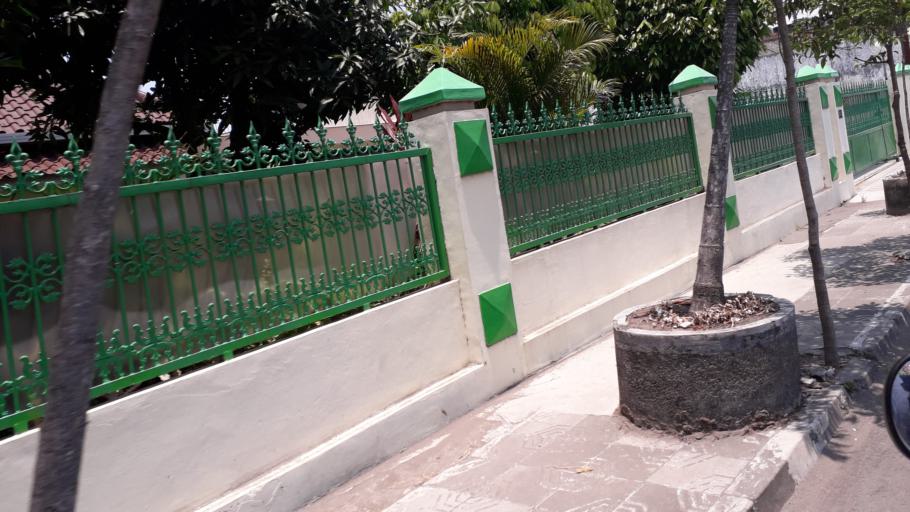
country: ID
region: Daerah Istimewa Yogyakarta
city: Yogyakarta
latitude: -7.7788
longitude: 110.3629
